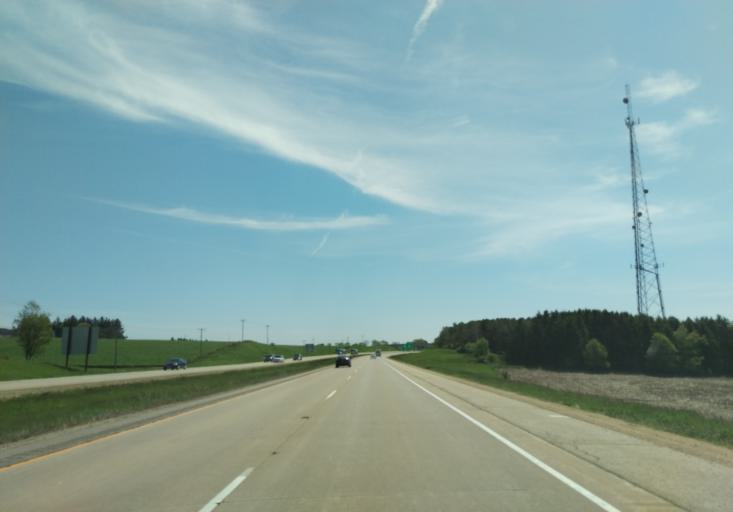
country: US
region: Wisconsin
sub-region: Dane County
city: Mount Horeb
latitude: 43.0041
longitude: -89.6886
